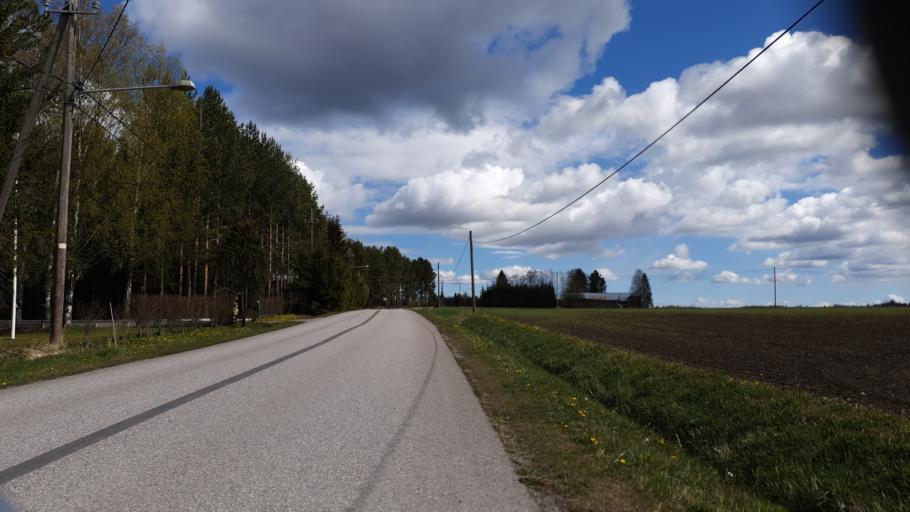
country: FI
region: Uusimaa
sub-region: Helsinki
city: Tuusula
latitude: 60.3947
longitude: 24.9173
